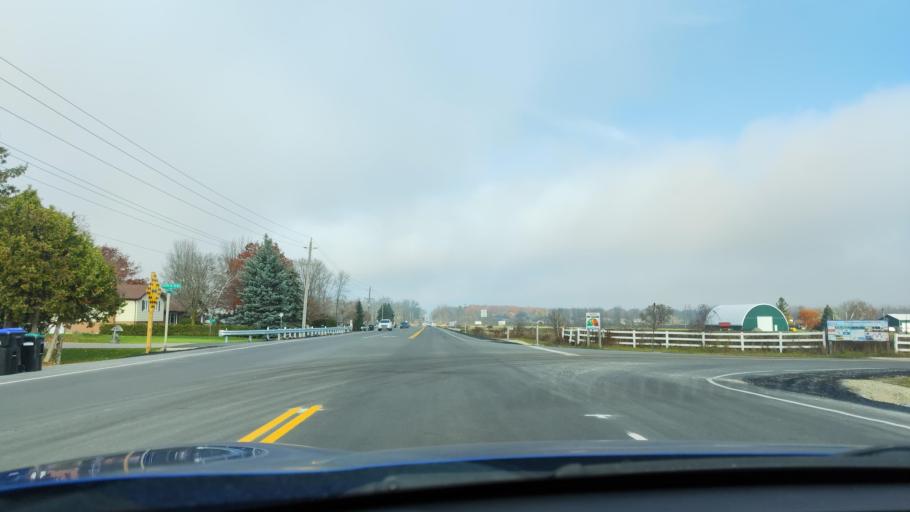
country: CA
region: Ontario
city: Wasaga Beach
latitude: 44.4562
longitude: -80.0716
